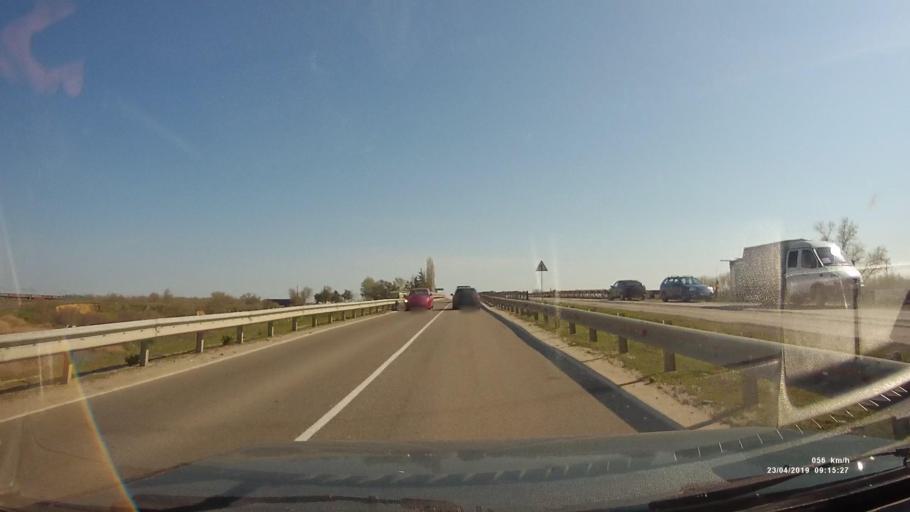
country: RU
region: Rostov
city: Proletarsk
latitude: 46.6318
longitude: 41.6642
